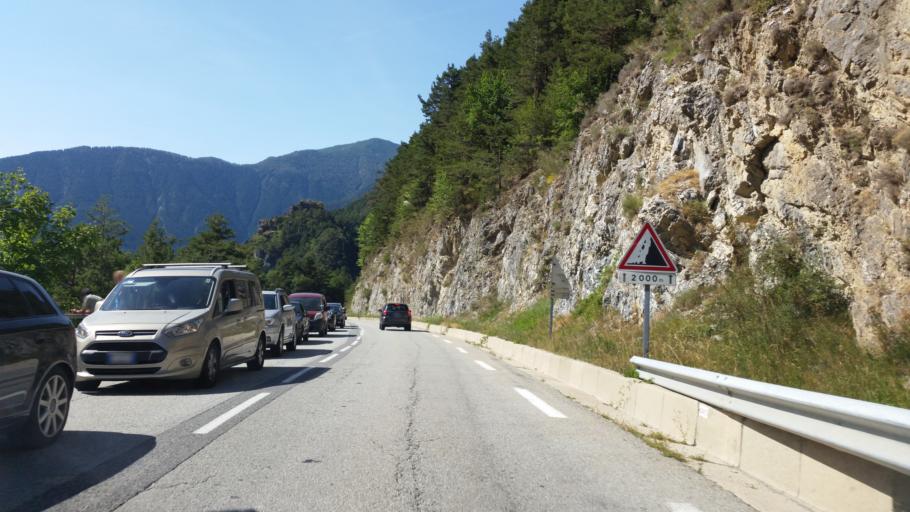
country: FR
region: Provence-Alpes-Cote d'Azur
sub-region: Departement des Alpes-Maritimes
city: Tende
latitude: 44.1330
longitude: 7.5670
